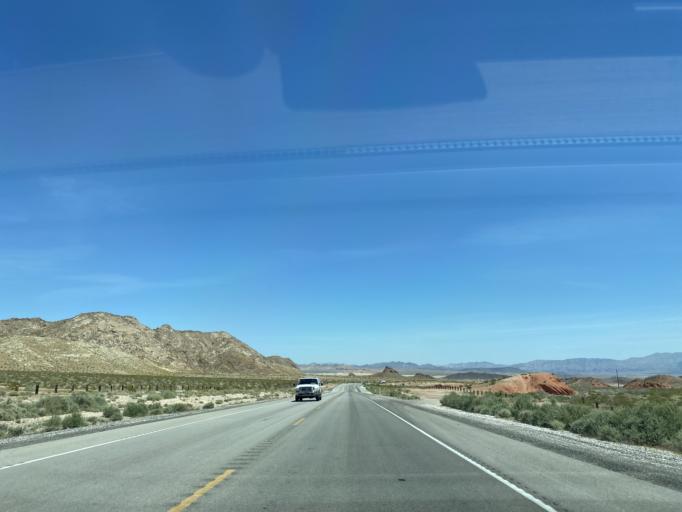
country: US
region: Nevada
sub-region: Clark County
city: Nellis Air Force Base
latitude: 36.2066
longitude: -114.9539
